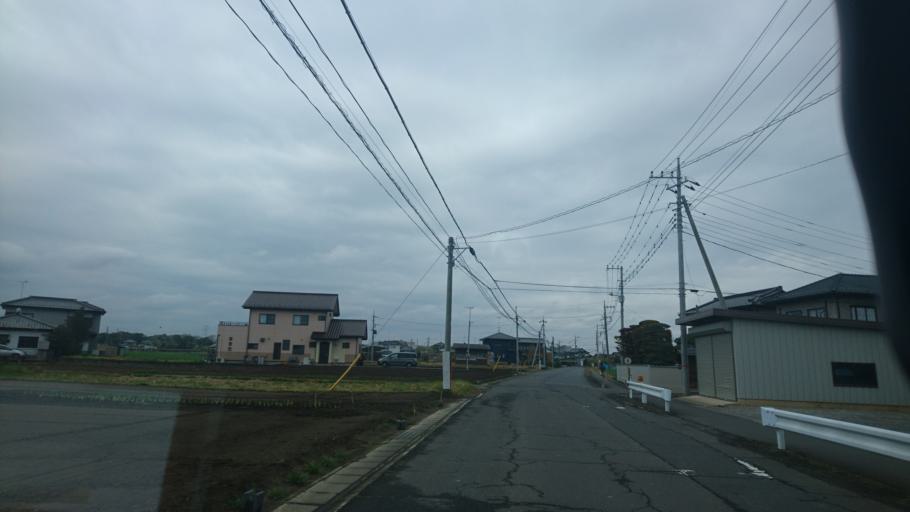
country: JP
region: Ibaraki
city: Ishige
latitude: 36.1384
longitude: 139.9623
